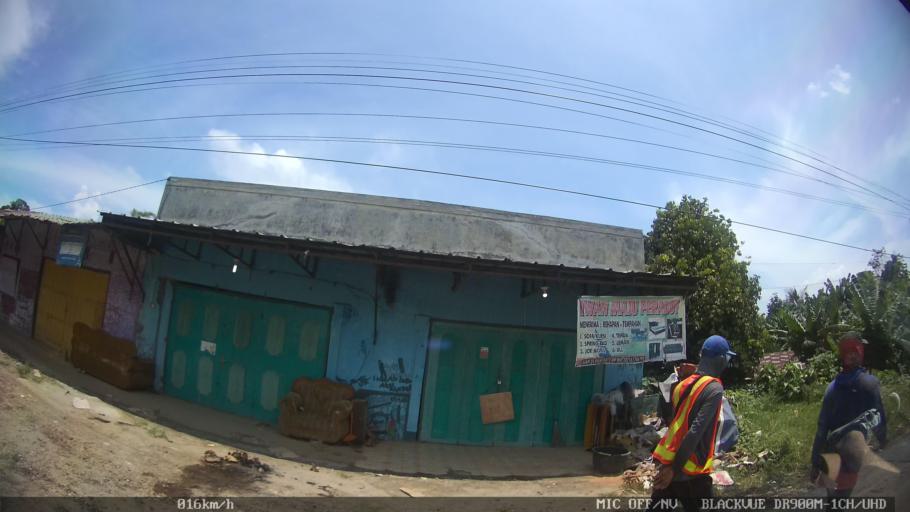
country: ID
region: North Sumatra
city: Binjai
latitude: 3.5916
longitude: 98.4977
